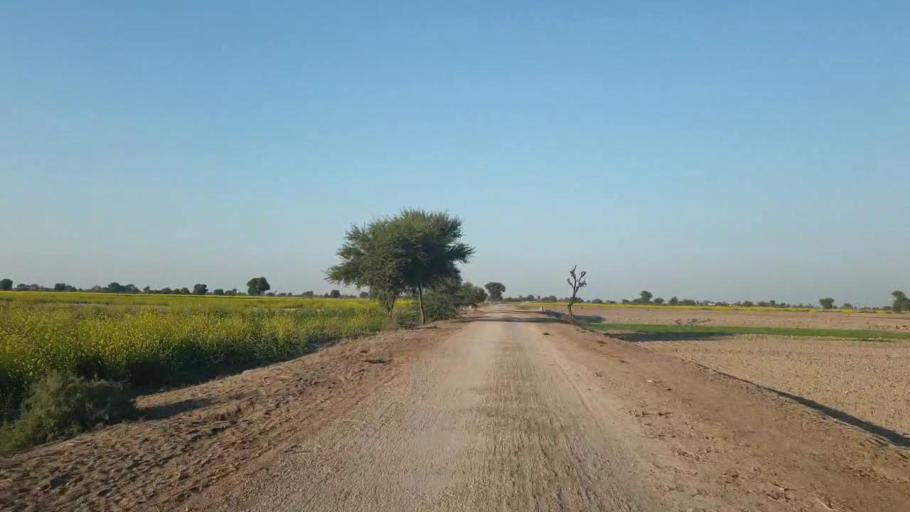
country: PK
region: Sindh
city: Shahpur Chakar
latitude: 26.0692
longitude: 68.6555
